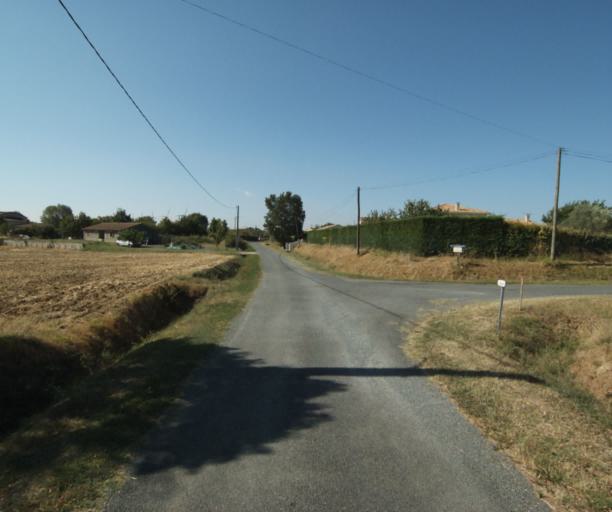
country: FR
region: Midi-Pyrenees
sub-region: Departement de la Haute-Garonne
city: Saint-Felix-Lauragais
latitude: 43.4835
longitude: 1.9175
